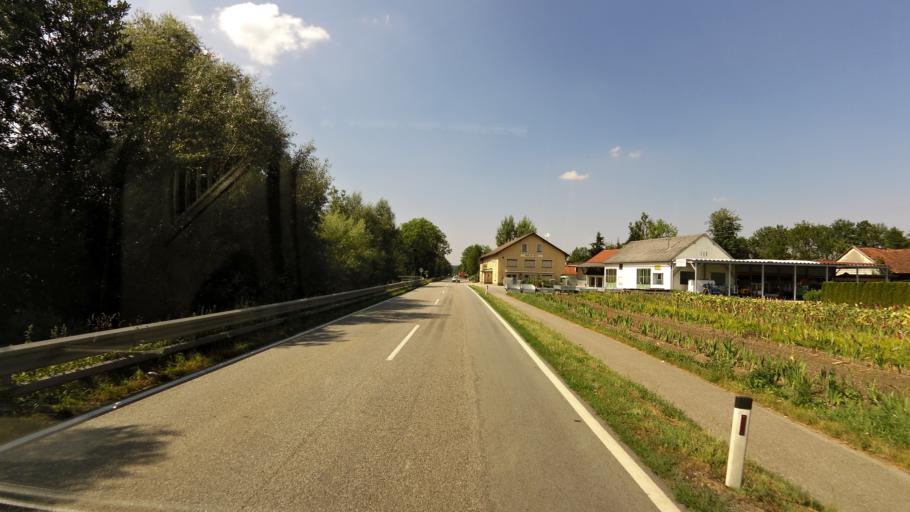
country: AT
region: Upper Austria
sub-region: Politischer Bezirk Braunau am Inn
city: Altheim
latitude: 48.1302
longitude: 13.1466
